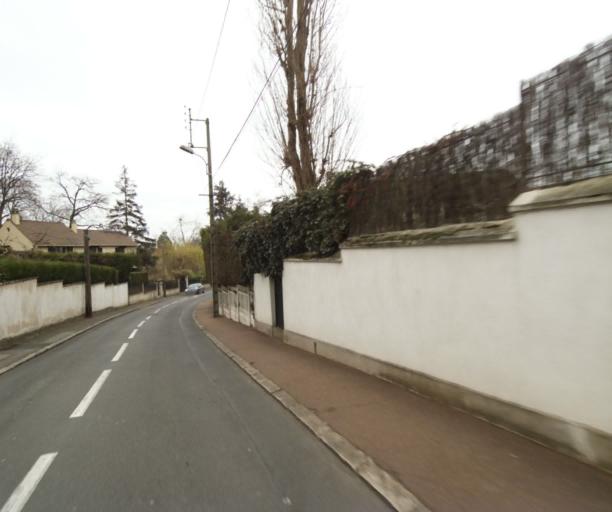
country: FR
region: Ile-de-France
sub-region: Departement des Hauts-de-Seine
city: Garches
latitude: 48.8492
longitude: 2.1906
